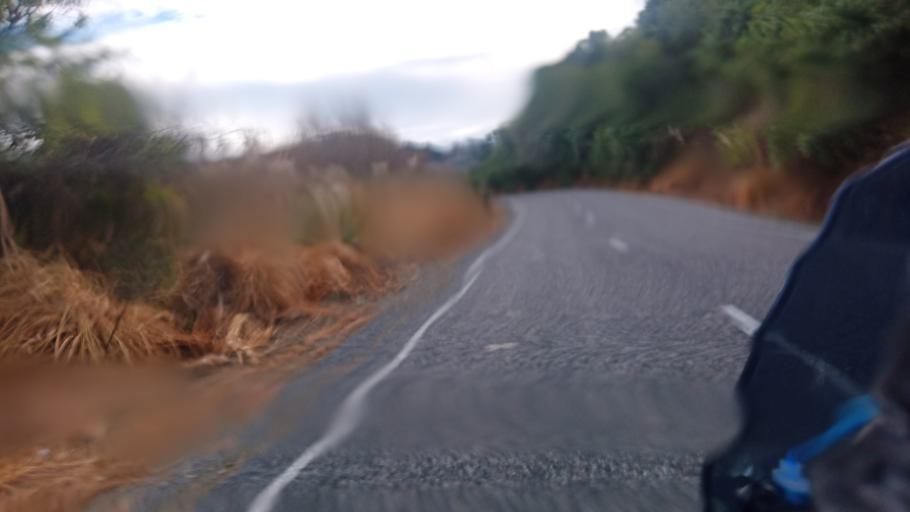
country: NZ
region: Gisborne
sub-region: Gisborne District
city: Gisborne
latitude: -38.4567
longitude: 177.8744
